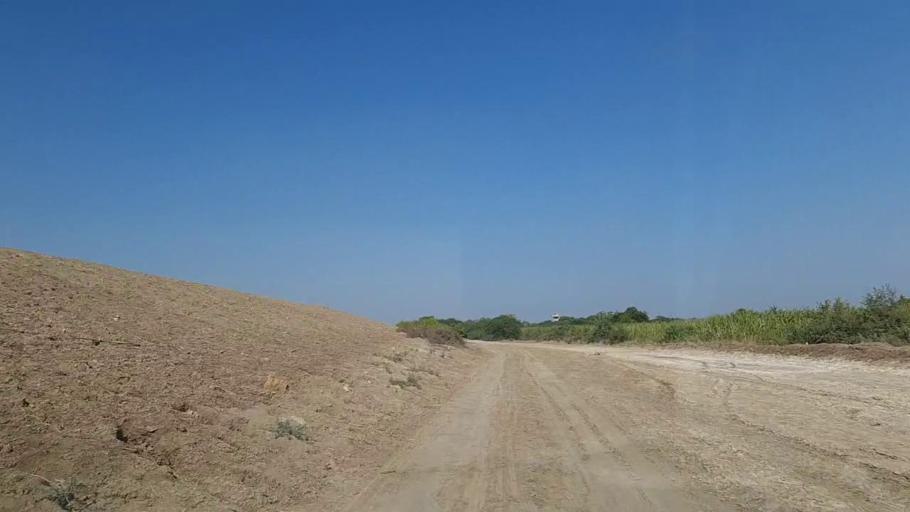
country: PK
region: Sindh
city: Chuhar Jamali
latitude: 24.4877
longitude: 68.0162
